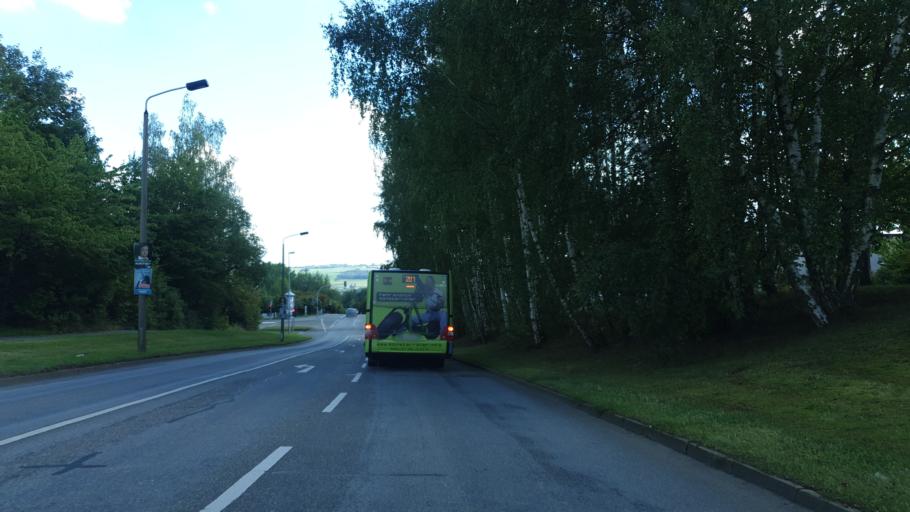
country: DE
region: Saxony
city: Neukirchen
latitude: 50.7844
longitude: 12.8765
